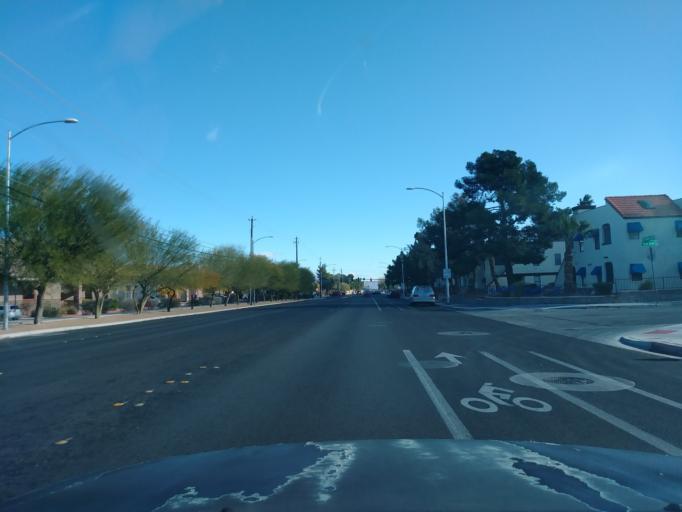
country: US
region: Nevada
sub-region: Clark County
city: Spring Valley
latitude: 36.1517
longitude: -115.2280
